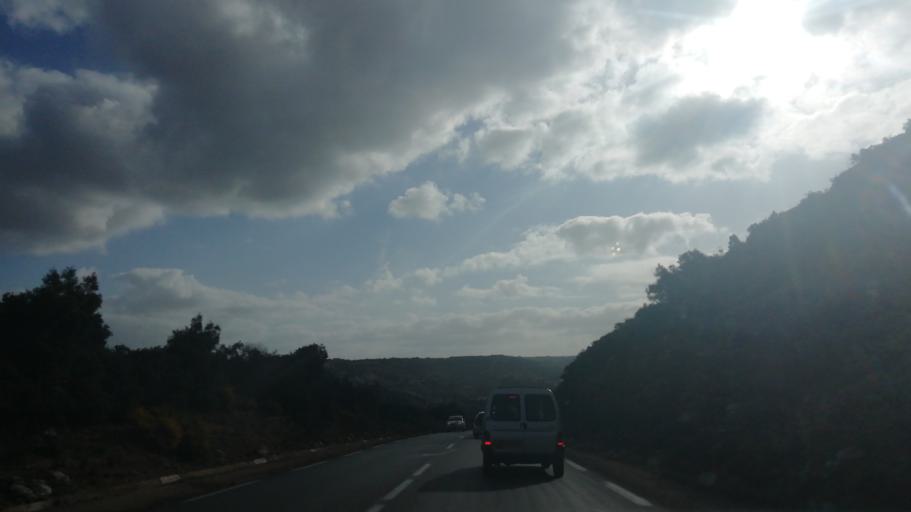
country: DZ
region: Relizane
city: Mazouna
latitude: 36.2386
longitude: 0.5328
